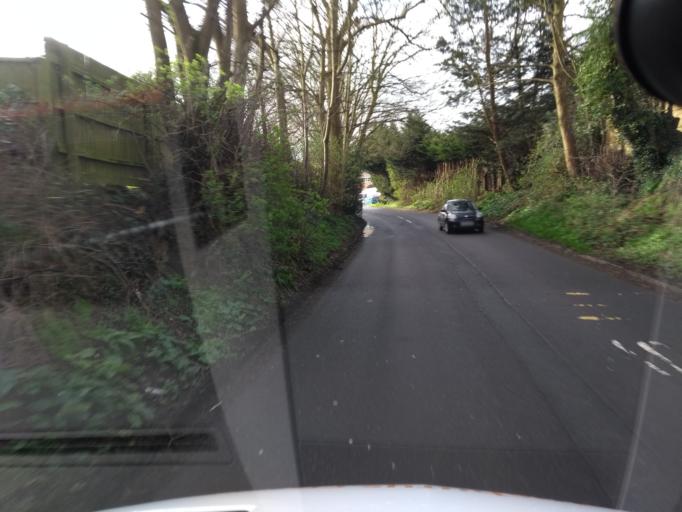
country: GB
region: England
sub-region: Somerset
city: Yeovil
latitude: 50.9553
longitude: -2.6484
